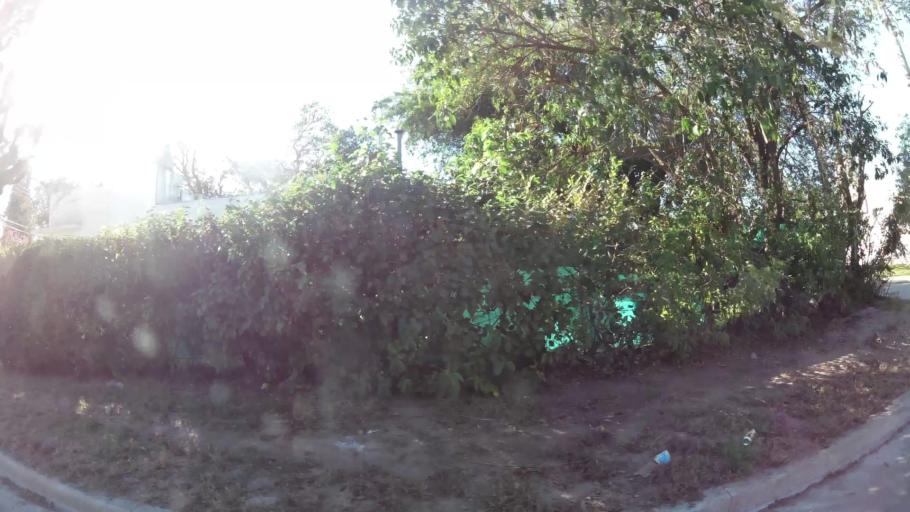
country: AR
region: Cordoba
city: Villa Allende
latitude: -31.3293
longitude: -64.2607
